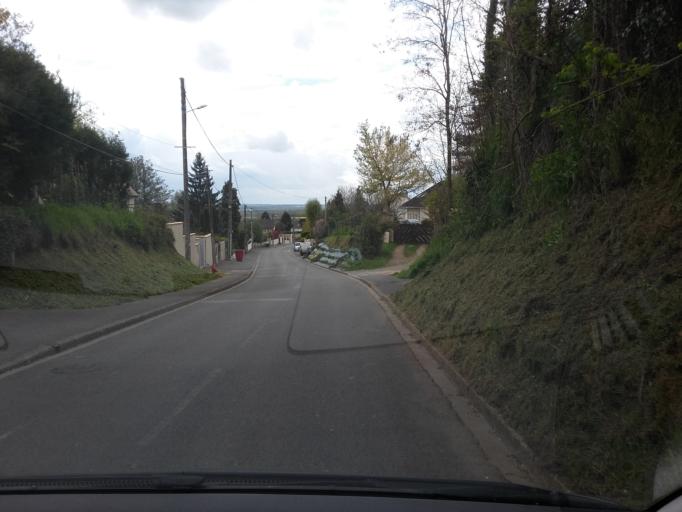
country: FR
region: Picardie
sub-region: Departement de l'Oise
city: Grandfresnoy
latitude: 49.3690
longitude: 2.6464
